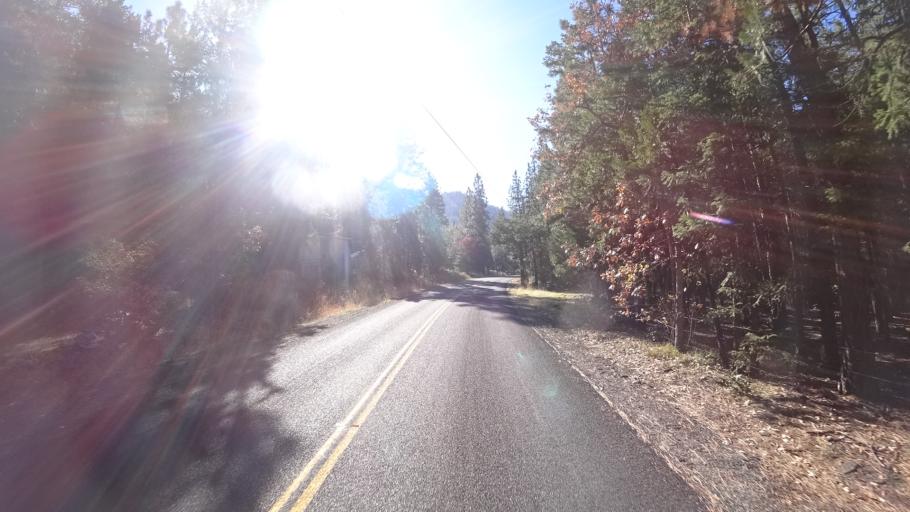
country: US
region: California
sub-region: Siskiyou County
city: Weed
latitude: 41.4266
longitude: -122.4987
